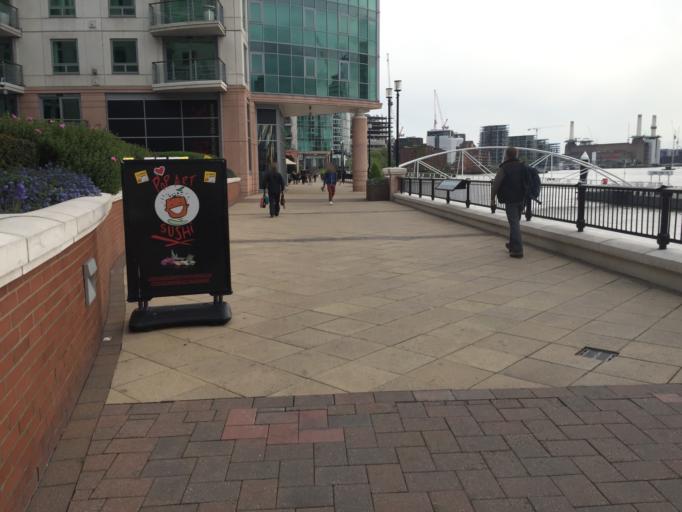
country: GB
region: England
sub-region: Greater London
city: City of Westminster
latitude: 51.4866
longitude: -0.1258
